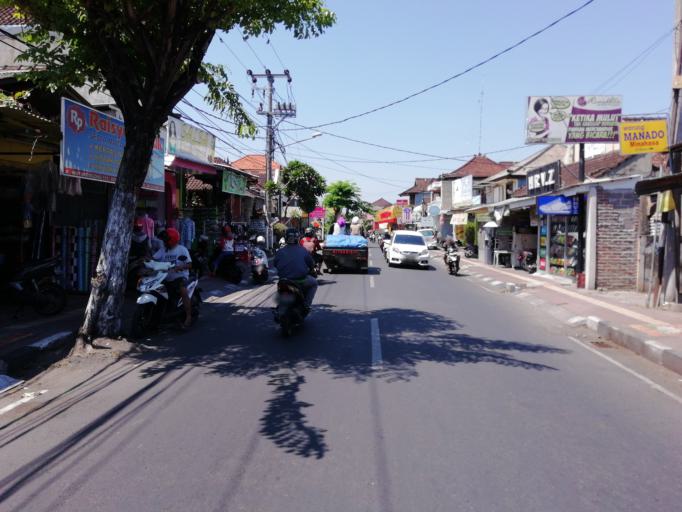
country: ID
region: Bali
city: Karyadharma
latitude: -8.6782
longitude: 115.2221
